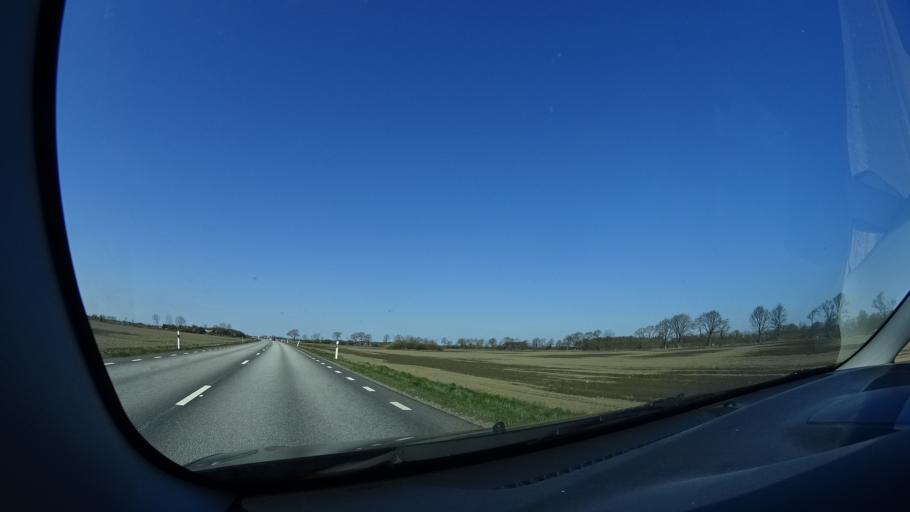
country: SE
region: Skane
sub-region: Angelholms Kommun
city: Strovelstorp
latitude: 56.2078
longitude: 12.7509
